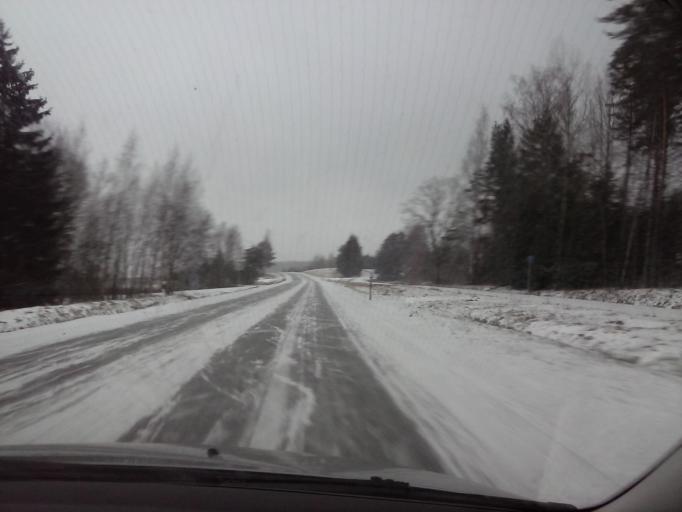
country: EE
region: Valgamaa
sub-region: Valga linn
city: Valga
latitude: 57.8481
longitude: 26.1307
